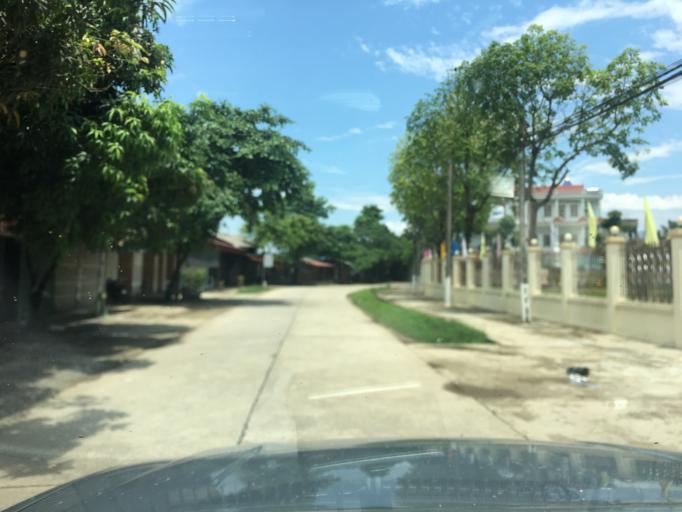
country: VN
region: Yen Bai
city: Son Thinh
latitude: 21.6395
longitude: 104.5018
